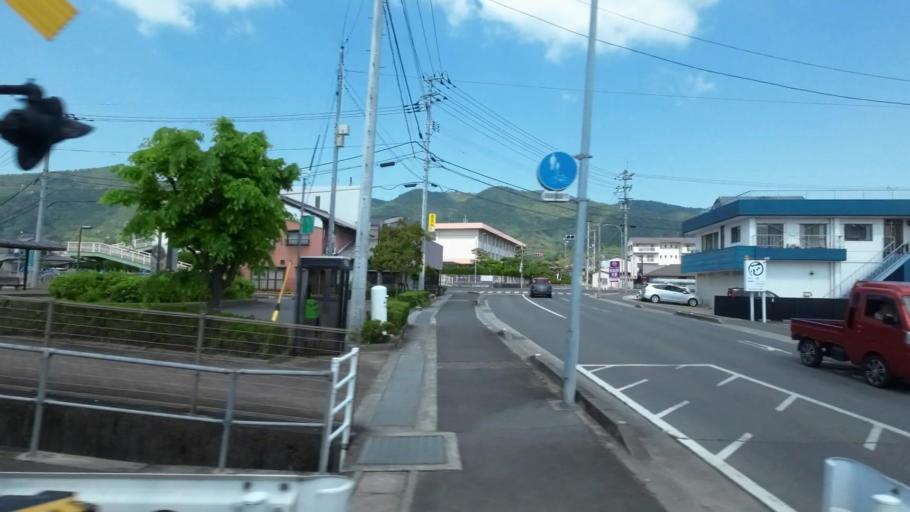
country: JP
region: Kagawa
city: Kan'onjicho
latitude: 34.1676
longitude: 133.6905
